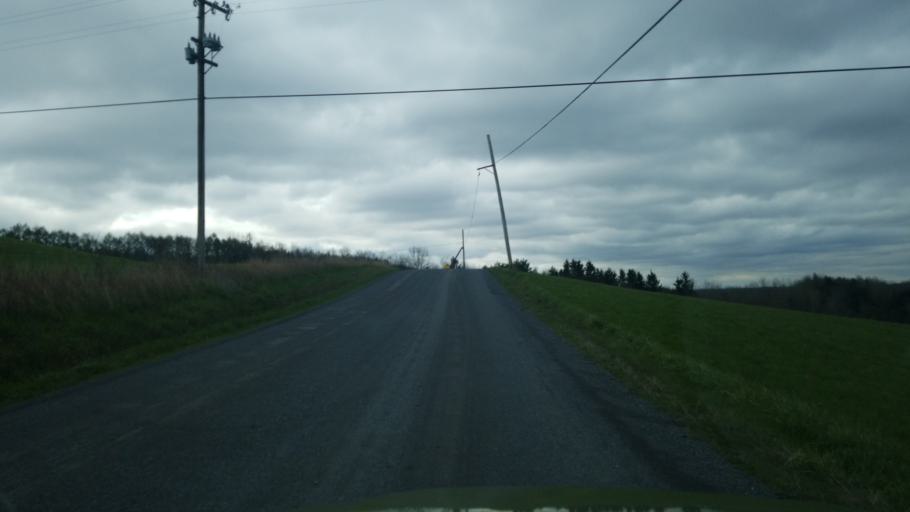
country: US
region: Pennsylvania
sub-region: Clearfield County
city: Clearfield
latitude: 41.0820
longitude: -78.3966
